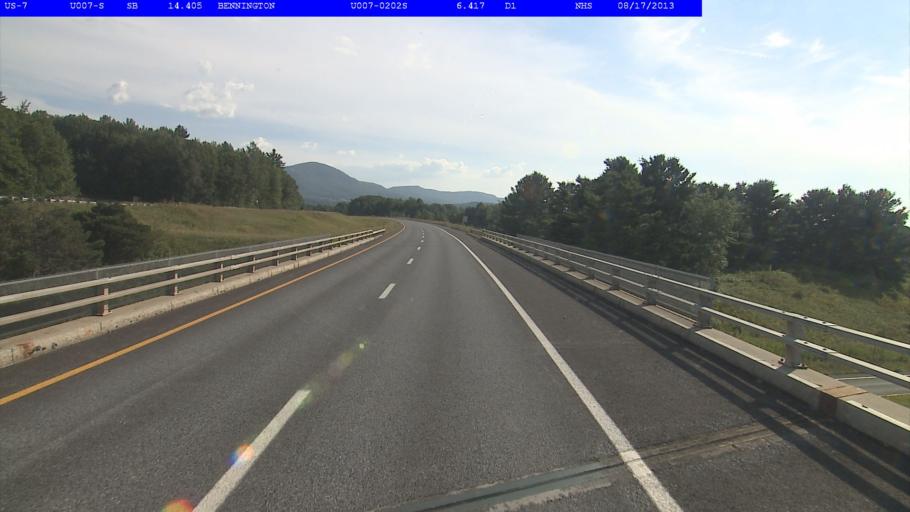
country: US
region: Vermont
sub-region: Bennington County
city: North Bennington
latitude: 42.9235
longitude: -73.2054
